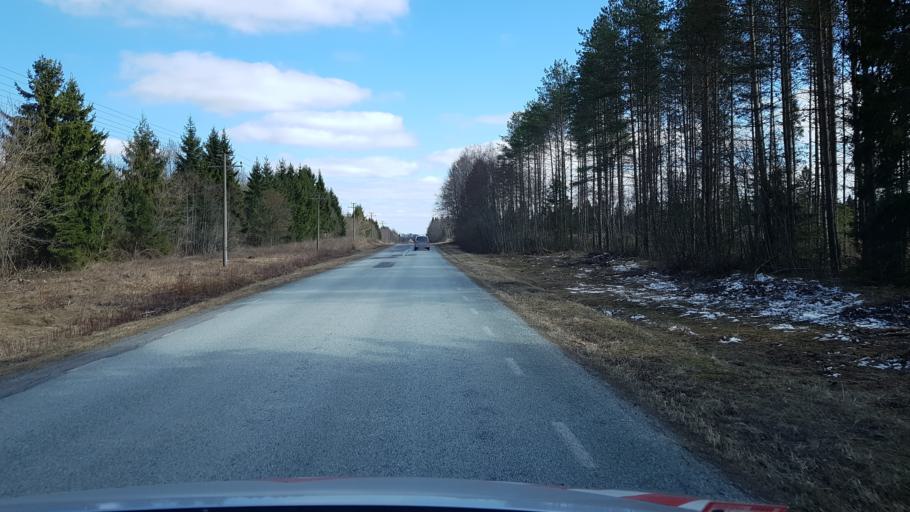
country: EE
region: Laeaene-Virumaa
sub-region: Tapa vald
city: Tapa
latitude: 59.2528
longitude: 25.7895
